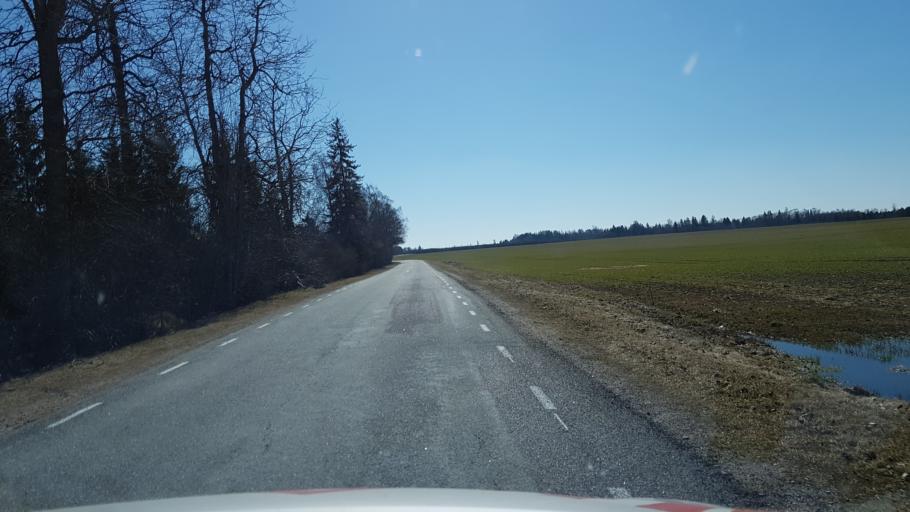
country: EE
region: Laeaene-Virumaa
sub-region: Rakke vald
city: Rakke
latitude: 59.0351
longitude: 26.3474
